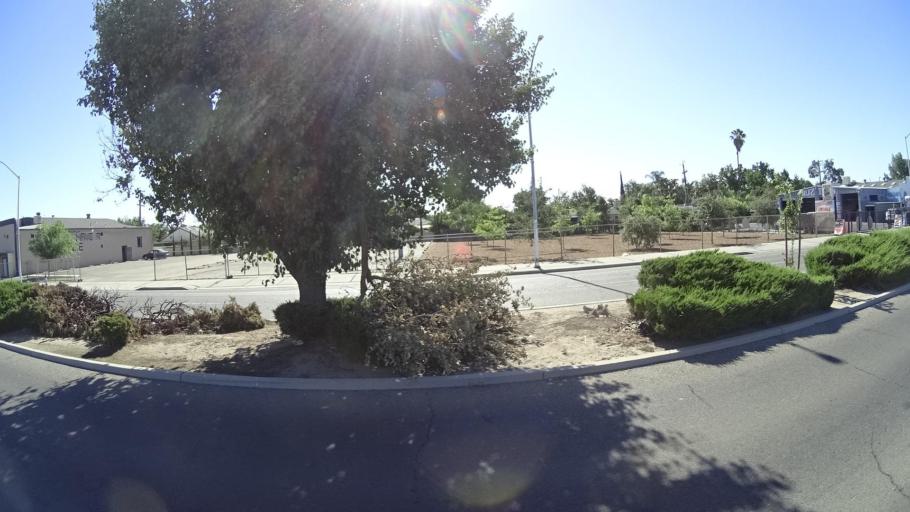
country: US
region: California
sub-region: Fresno County
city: Fresno
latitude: 36.7093
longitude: -119.7909
